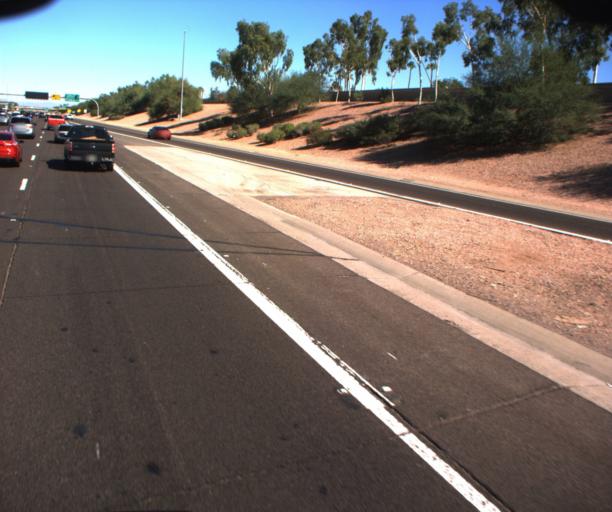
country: US
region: Arizona
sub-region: Maricopa County
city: Tempe
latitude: 33.3967
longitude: -111.8909
